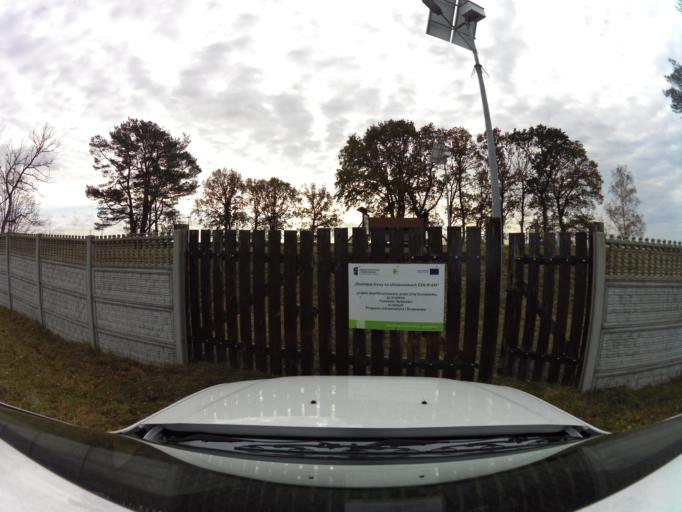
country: PL
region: West Pomeranian Voivodeship
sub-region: Powiat gryficki
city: Karnice
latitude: 54.0519
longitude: 15.0938
